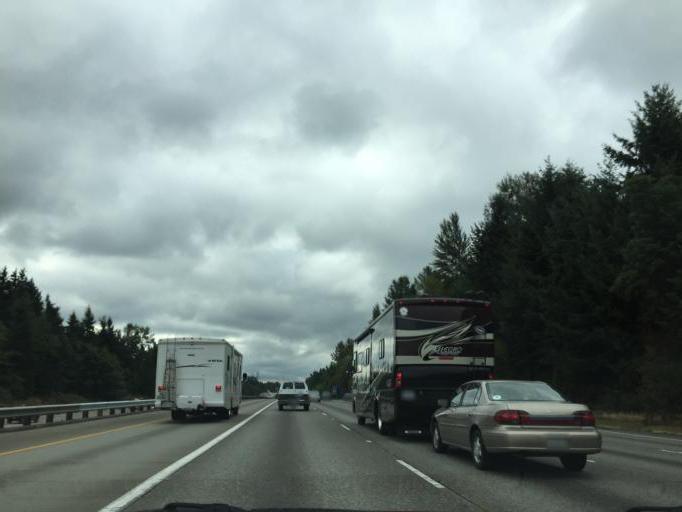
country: US
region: Washington
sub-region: King County
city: Lakeland North
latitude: 47.3343
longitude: -122.2938
